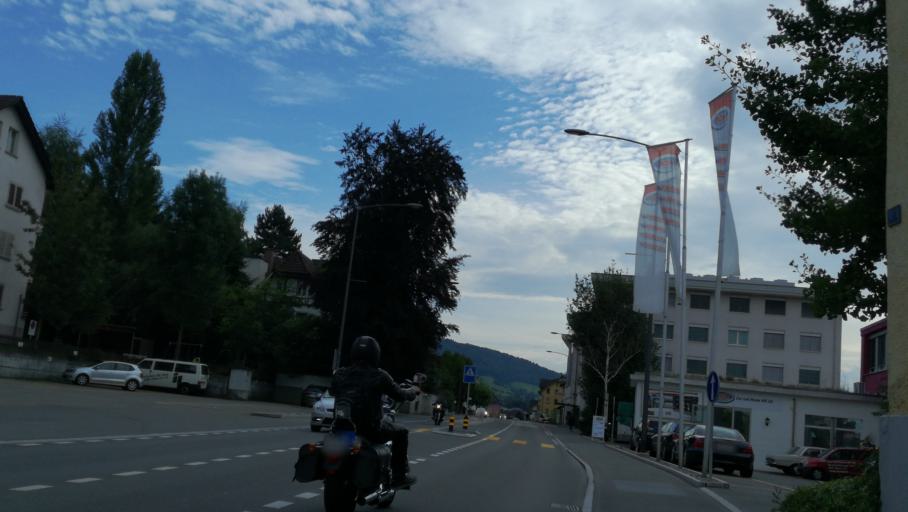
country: CH
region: Lucerne
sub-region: Lucerne-Land District
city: Root
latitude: 47.1189
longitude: 8.3929
